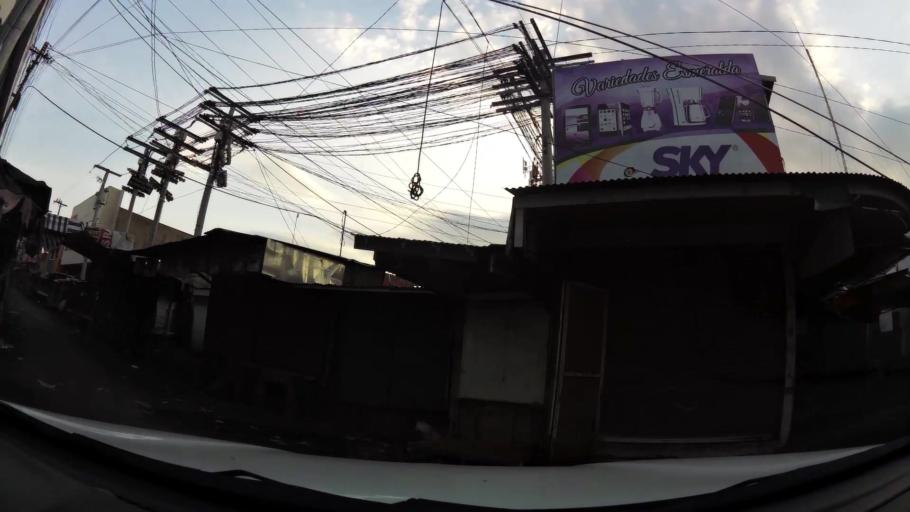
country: NI
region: Managua
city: Managua
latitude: 12.1477
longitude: -86.2576
